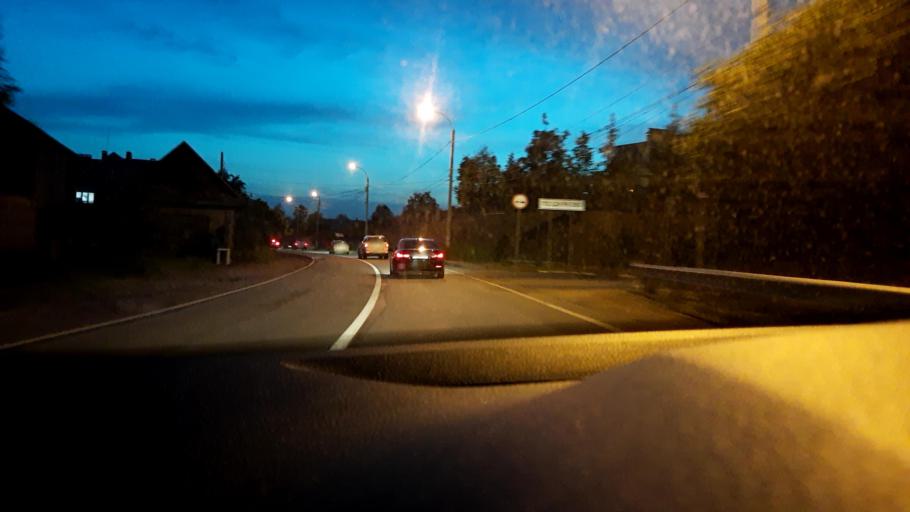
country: RU
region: Moskovskaya
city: Opalikha
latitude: 55.7886
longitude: 37.2240
